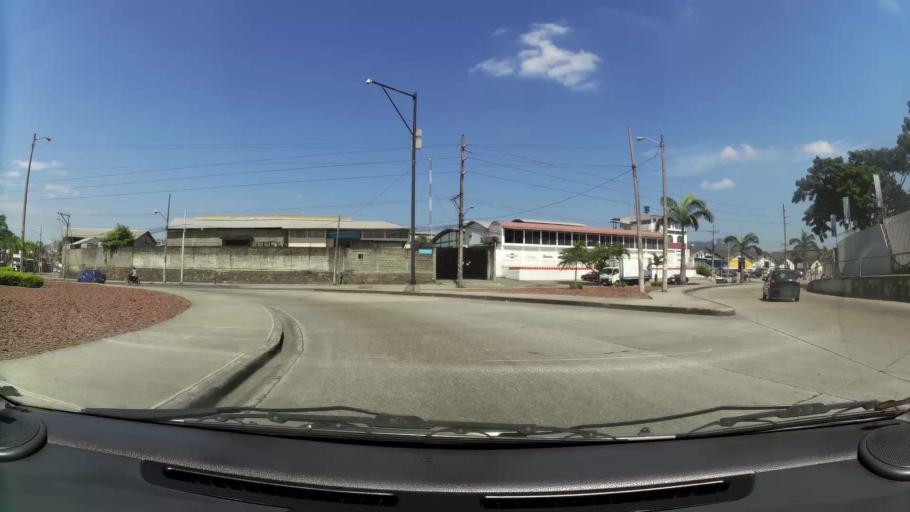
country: EC
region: Guayas
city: Guayaquil
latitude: -2.1307
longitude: -79.9304
